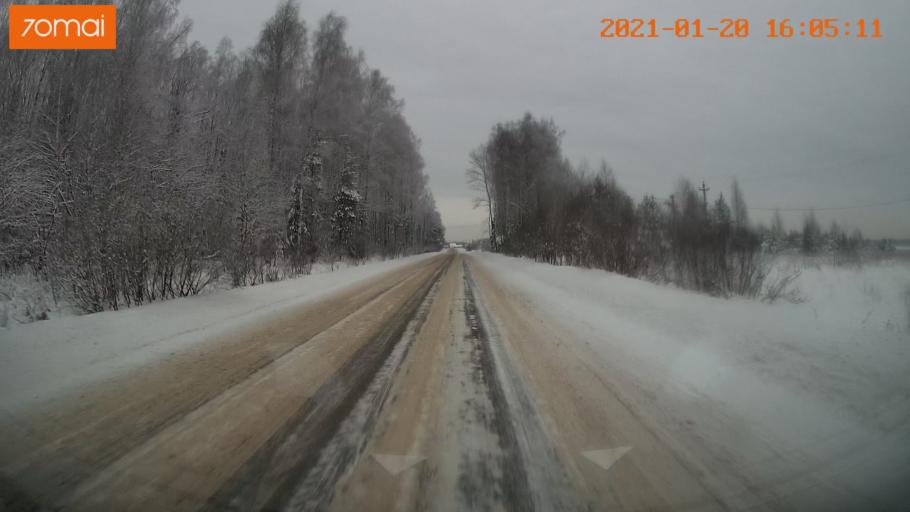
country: RU
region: Vladimir
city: Sudogda
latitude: 56.0633
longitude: 40.8089
